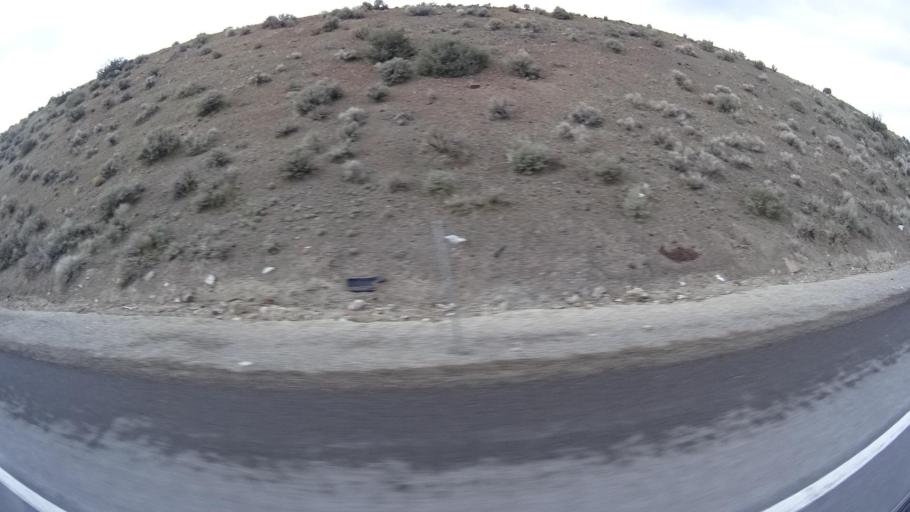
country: US
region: Nevada
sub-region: Storey County
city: Virginia City
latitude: 39.3357
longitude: -119.7806
